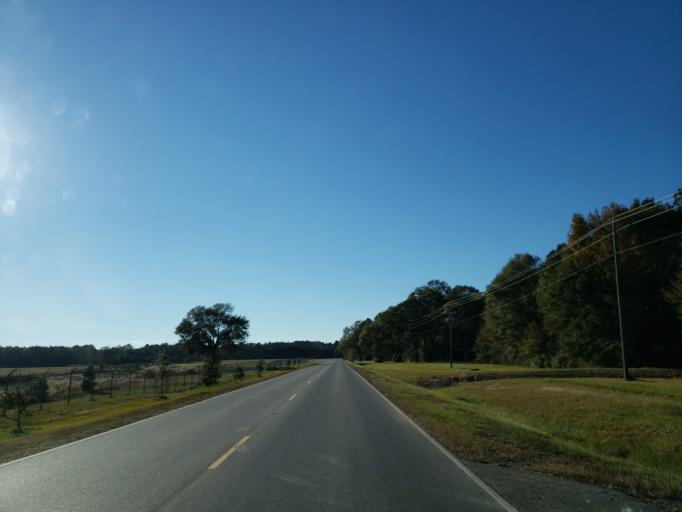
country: US
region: Mississippi
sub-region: Forrest County
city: Hattiesburg
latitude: 31.2733
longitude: -89.2563
